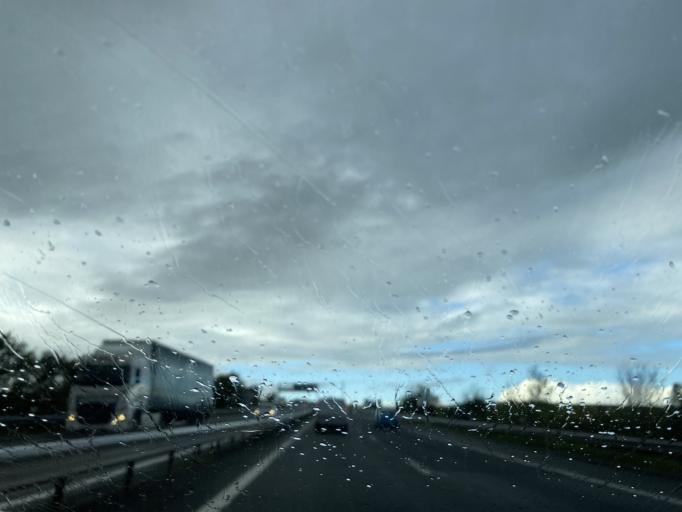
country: FR
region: Auvergne
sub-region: Departement de l'Allier
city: Vallon-en-Sully
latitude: 46.5102
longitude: 2.6037
